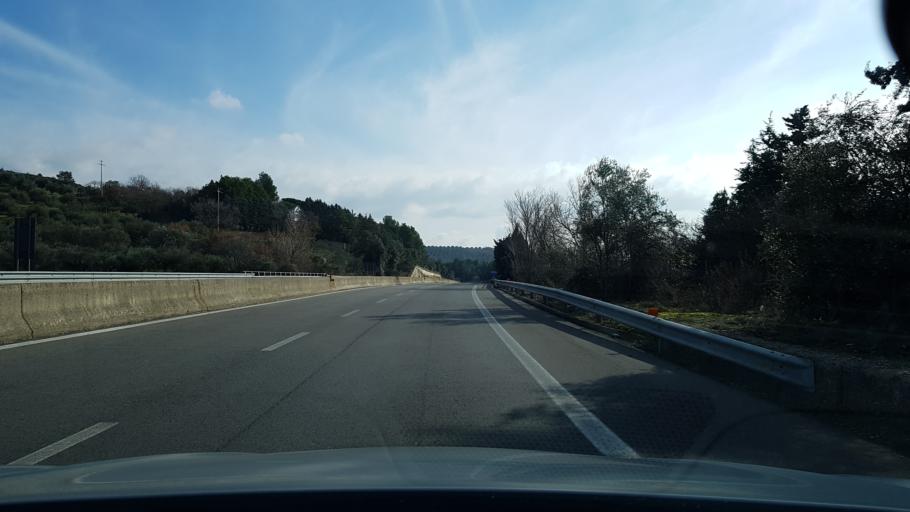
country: IT
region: Umbria
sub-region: Provincia di Perugia
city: Passignano sul Trasimeno
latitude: 43.1967
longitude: 12.1301
